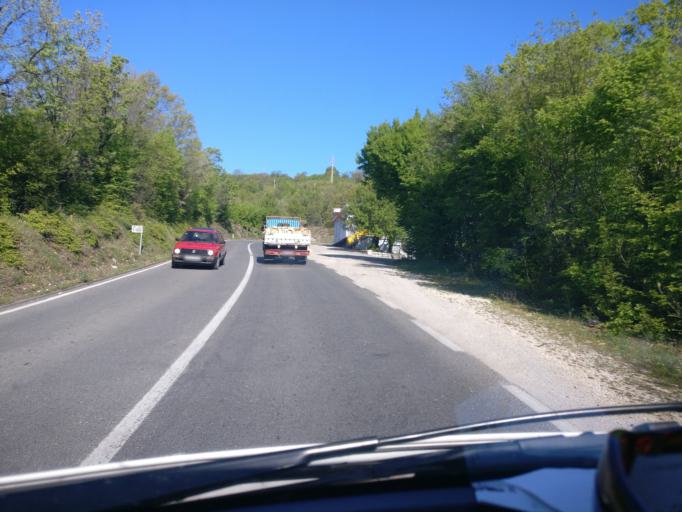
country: BA
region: Federation of Bosnia and Herzegovina
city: Crnici
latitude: 43.1024
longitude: 17.9050
